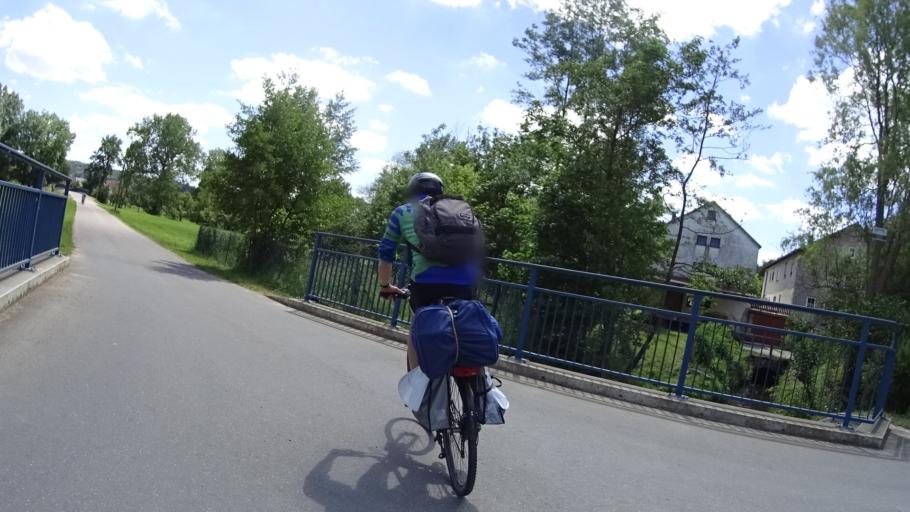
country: DE
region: Bavaria
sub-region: Regierungsbezirk Unterfranken
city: Bieberehren
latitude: 49.5160
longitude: 10.0029
